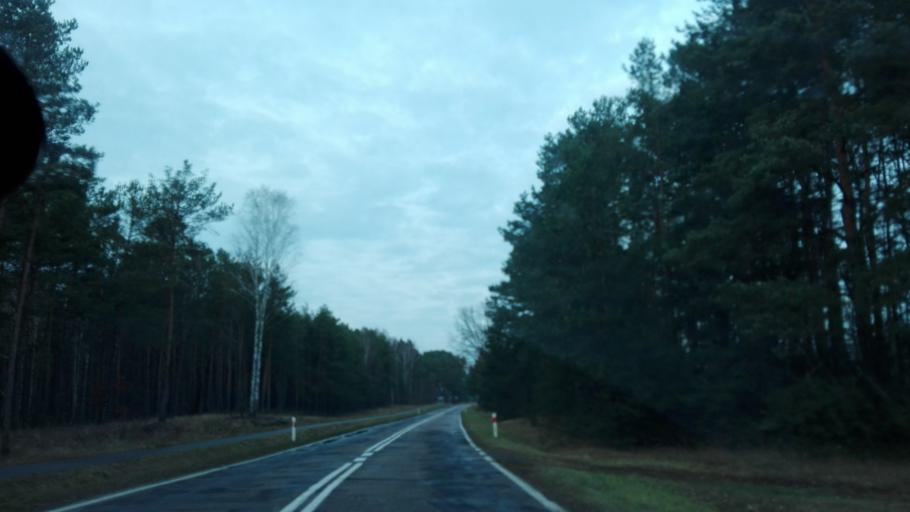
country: PL
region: Lublin Voivodeship
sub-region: Powiat bialski
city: Slawatycze
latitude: 51.7092
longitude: 23.5024
